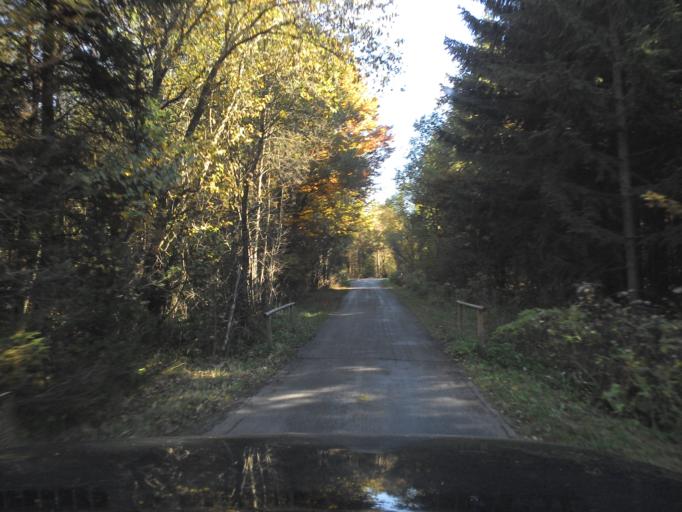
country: DE
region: Bavaria
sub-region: Upper Bavaria
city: Seeshaupt
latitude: 47.8115
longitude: 11.3324
